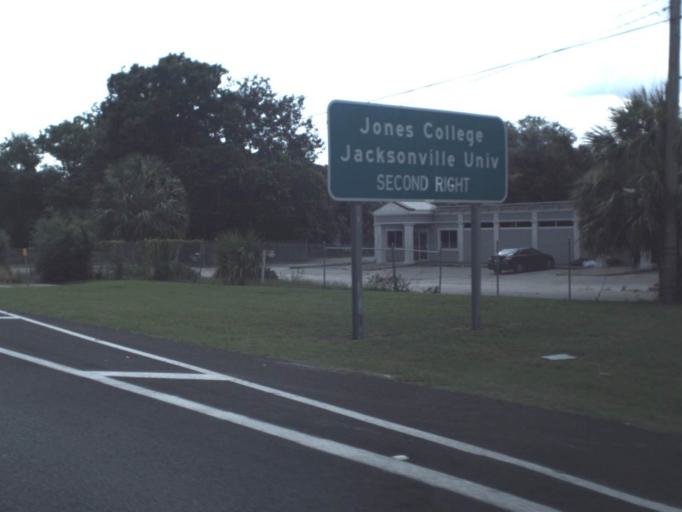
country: US
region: Florida
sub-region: Duval County
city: Jacksonville
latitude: 30.3272
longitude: -81.6079
